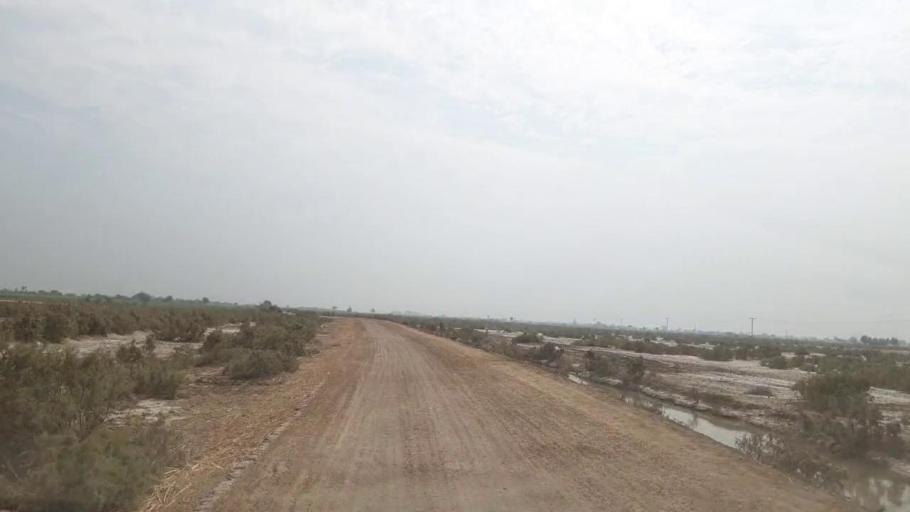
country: PK
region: Sindh
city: Mirpur Khas
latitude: 25.5470
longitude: 69.1252
